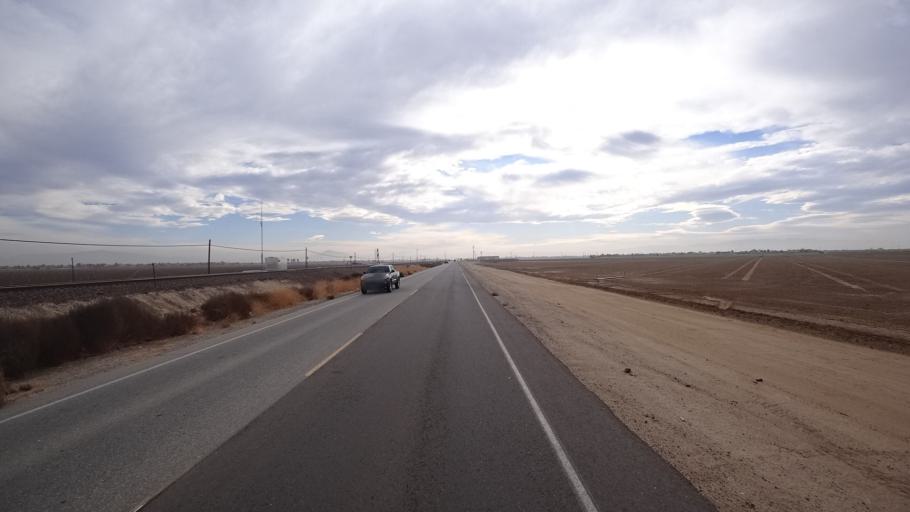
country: US
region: California
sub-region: Kern County
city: Rosedale
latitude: 35.4150
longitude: -119.1668
